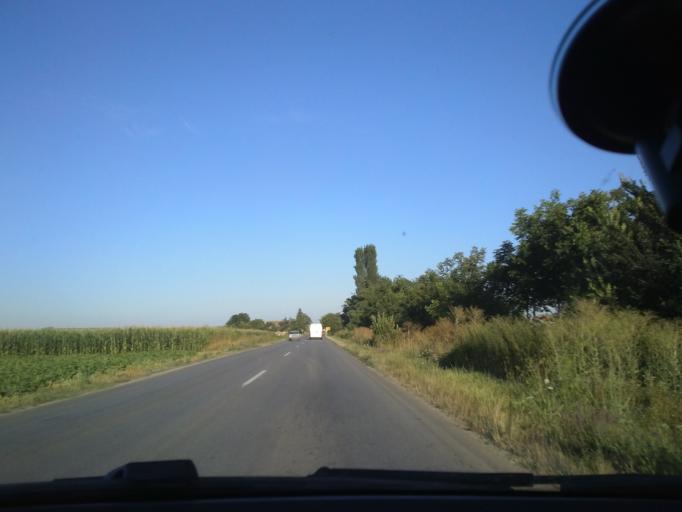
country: RS
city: Maglic
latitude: 45.3987
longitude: 19.4480
